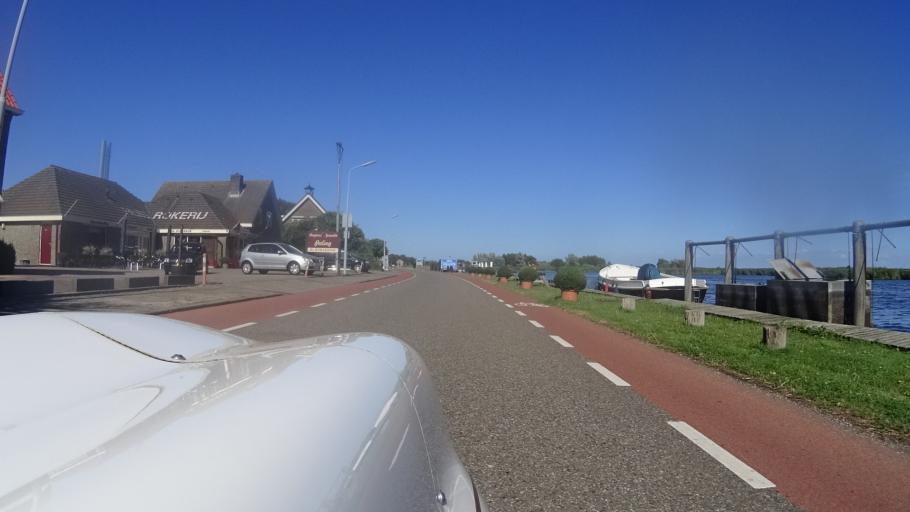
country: NL
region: South Holland
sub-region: Gemeente Kaag en Braassem
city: Leimuiden
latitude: 52.2408
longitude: 4.6858
